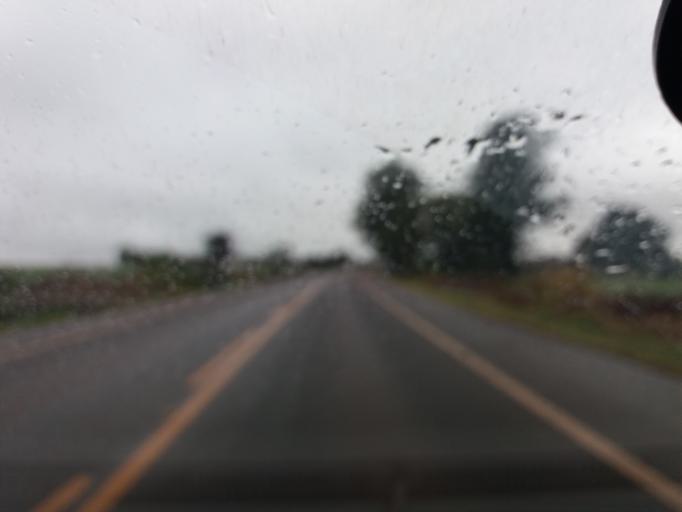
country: BR
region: Parana
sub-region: Moreira Sales
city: Moreira Sales
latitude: -24.3342
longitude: -52.6885
